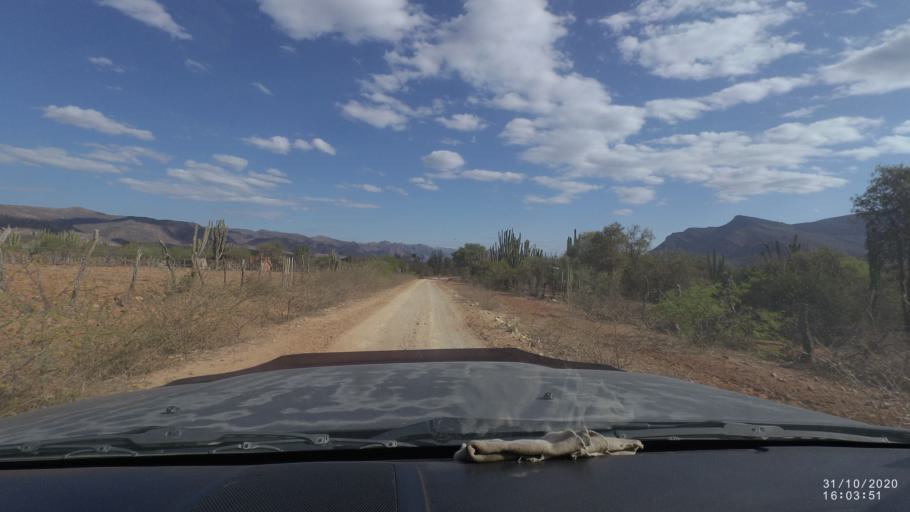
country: BO
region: Chuquisaca
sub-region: Provincia Zudanez
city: Mojocoya
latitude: -18.3553
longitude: -64.6514
